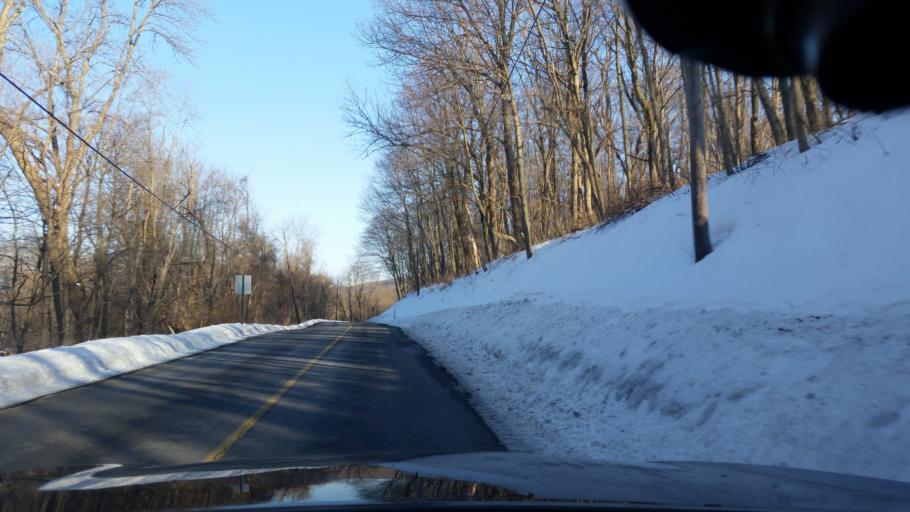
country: US
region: Pennsylvania
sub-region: Perry County
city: Marysville
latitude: 40.3247
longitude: -76.9969
